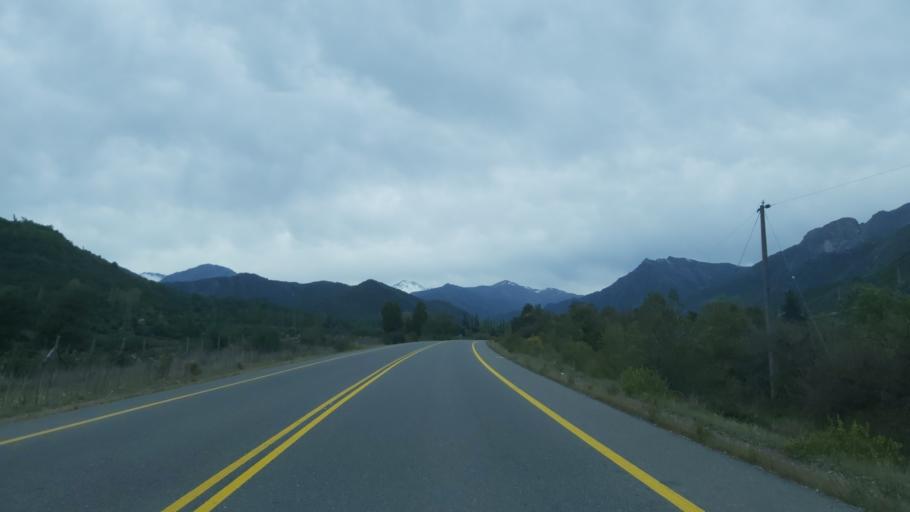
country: CL
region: Maule
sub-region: Provincia de Linares
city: Colbun
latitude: -35.7408
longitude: -71.0092
